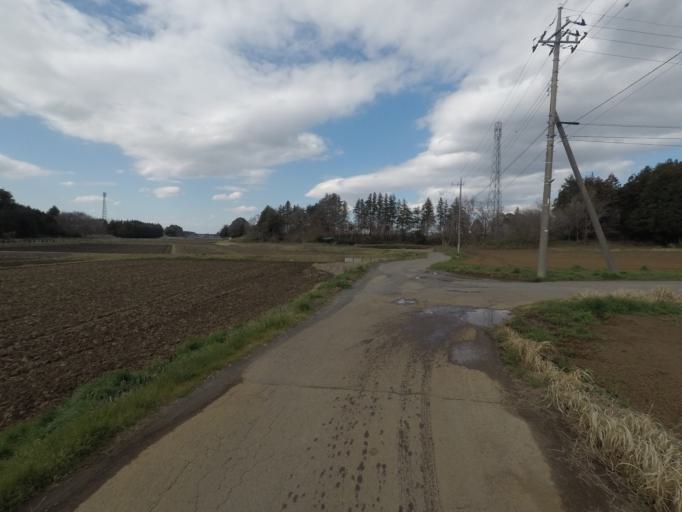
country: JP
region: Ibaraki
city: Ushiku
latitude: 36.0090
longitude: 140.1177
